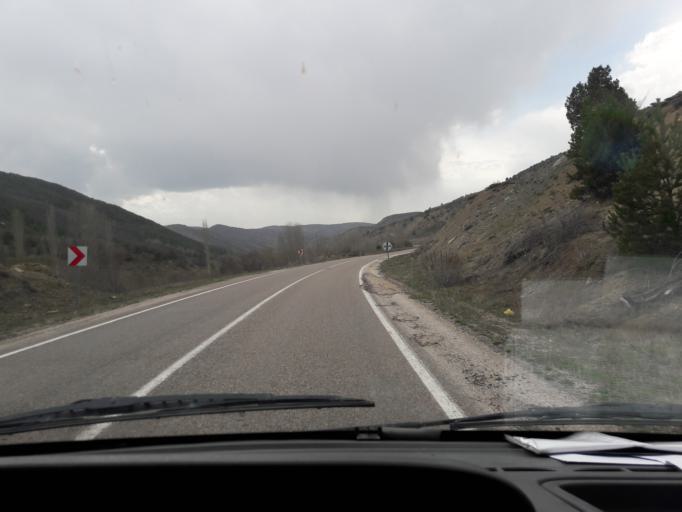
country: TR
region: Giresun
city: Alucra
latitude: 40.2731
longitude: 38.8600
